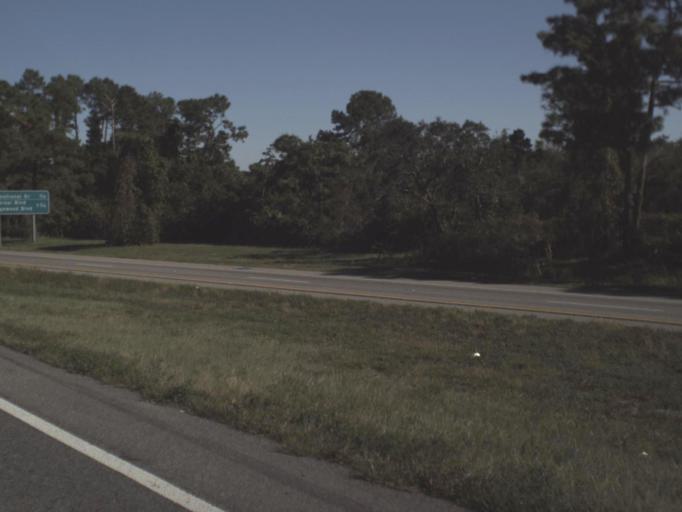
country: US
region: Florida
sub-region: Orange County
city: Williamsburg
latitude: 28.4204
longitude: -81.4713
